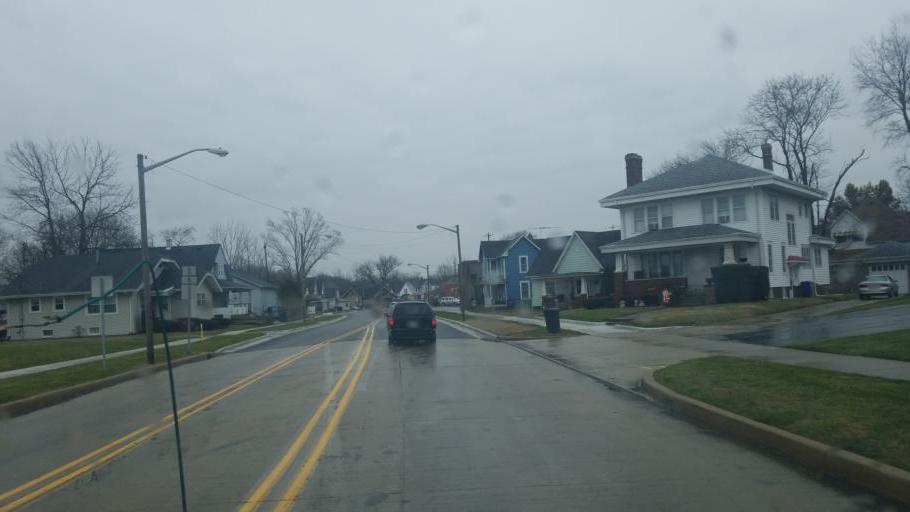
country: US
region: Indiana
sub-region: Shelby County
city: Shelbyville
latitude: 39.5171
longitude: -85.7769
